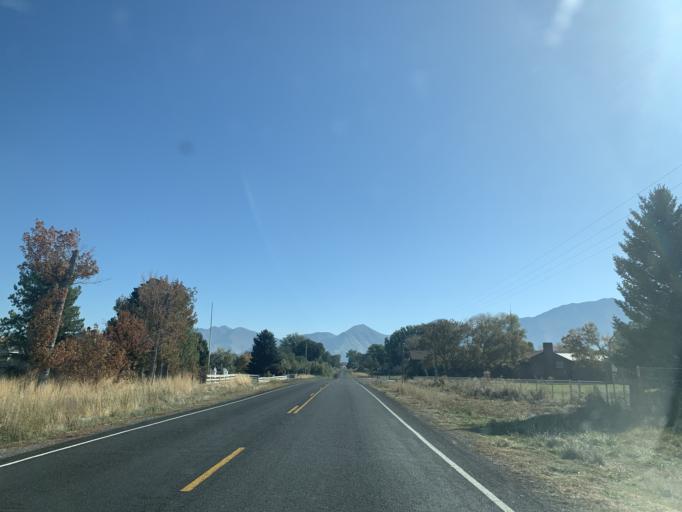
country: US
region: Utah
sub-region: Utah County
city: West Mountain
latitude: 40.0410
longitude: -111.7803
